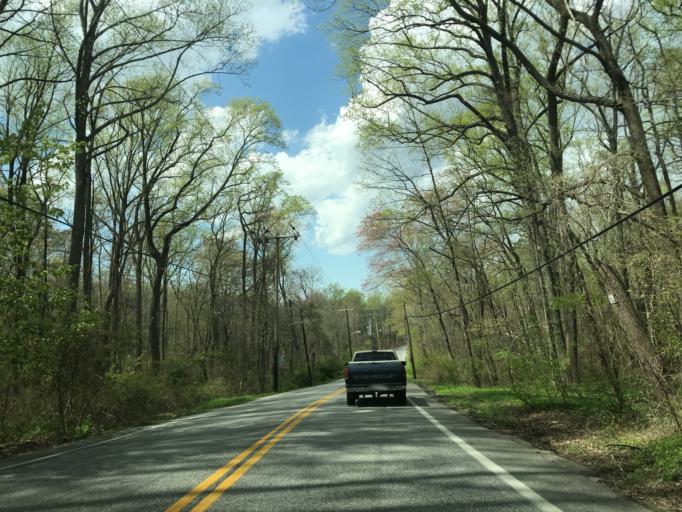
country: US
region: Maryland
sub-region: Anne Arundel County
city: Odenton
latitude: 39.0999
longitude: -76.6846
